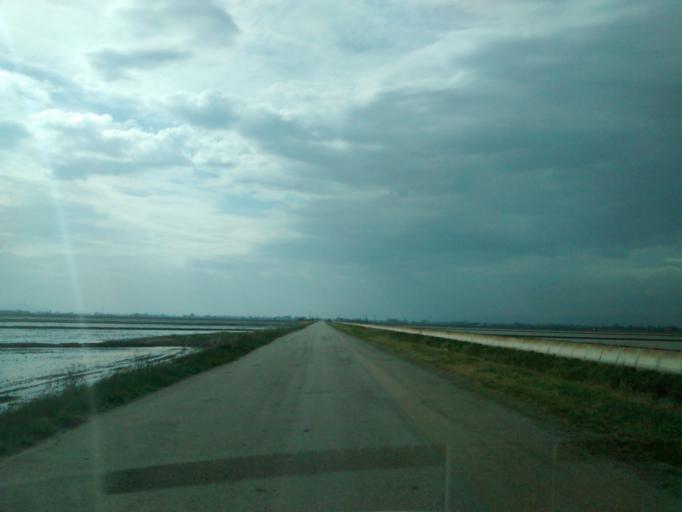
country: ES
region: Catalonia
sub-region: Provincia de Tarragona
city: Deltebre
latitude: 40.6943
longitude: 0.7680
